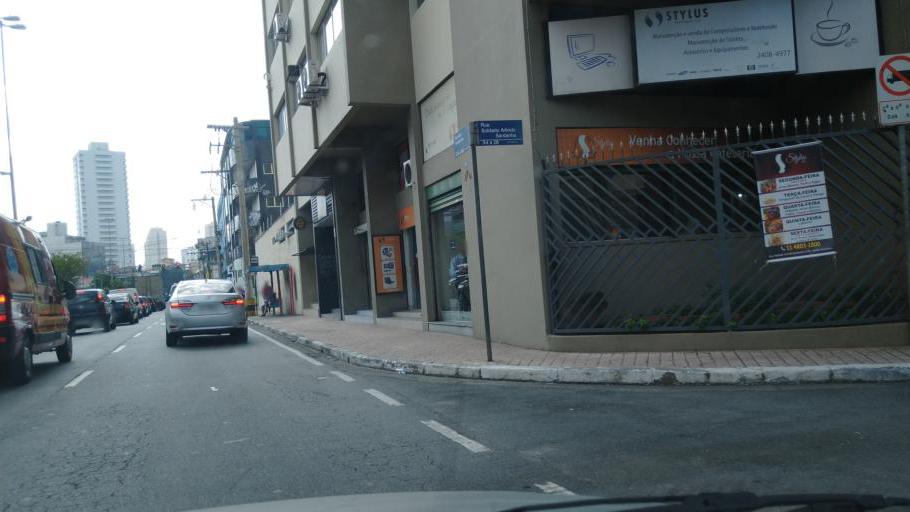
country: BR
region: Sao Paulo
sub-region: Guarulhos
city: Guarulhos
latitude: -23.4692
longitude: -46.5348
